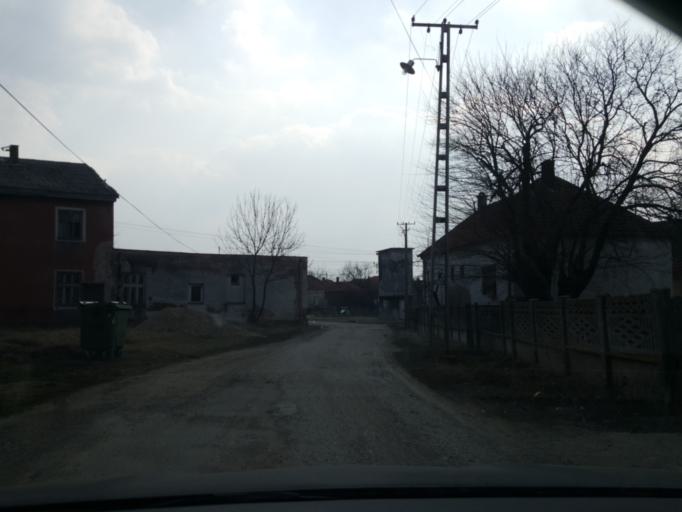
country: RS
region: Central Serbia
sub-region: Nisavski Okrug
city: Aleksinac
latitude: 43.4506
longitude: 21.7906
